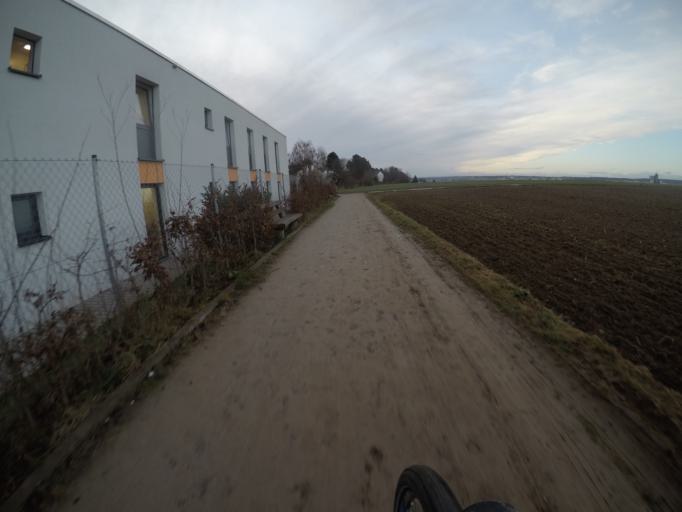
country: DE
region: Baden-Wuerttemberg
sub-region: Regierungsbezirk Stuttgart
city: Ostfildern
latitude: 48.7223
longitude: 9.2048
